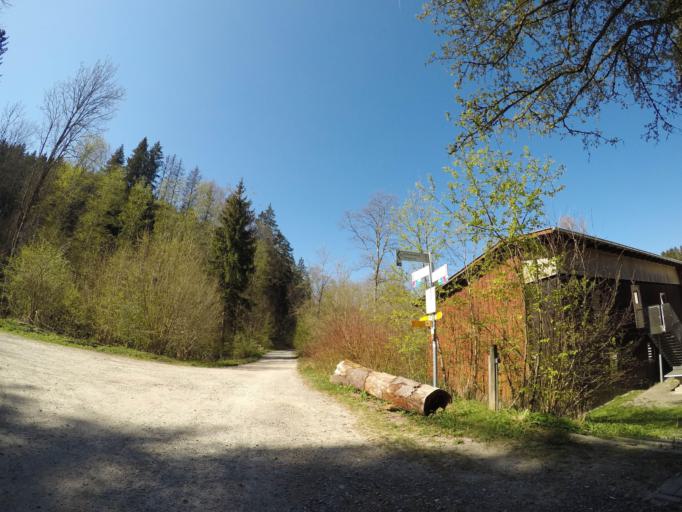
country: DE
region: Baden-Wuerttemberg
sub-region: Tuebingen Region
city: Horgenzell
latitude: 47.8164
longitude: 9.4637
